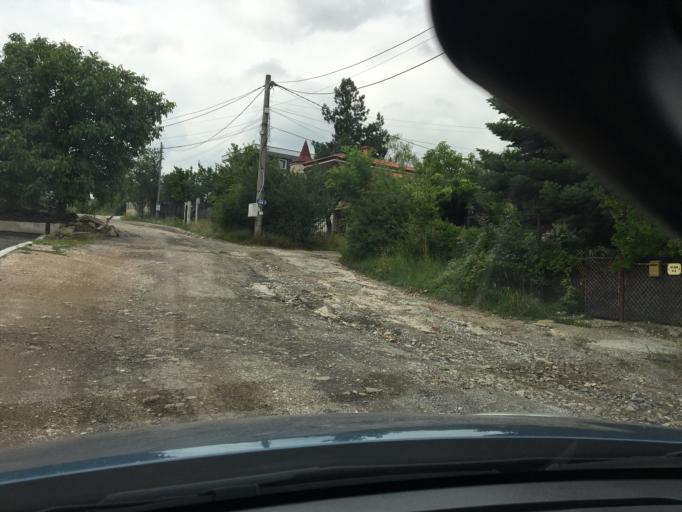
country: BG
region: Sofia-Capital
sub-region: Stolichna Obshtina
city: Sofia
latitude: 42.6168
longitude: 23.3618
